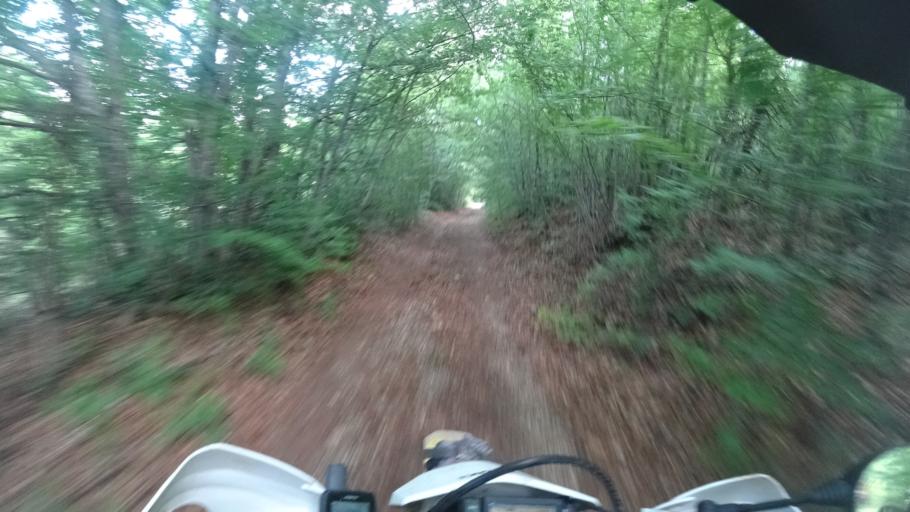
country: HR
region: Zadarska
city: Gracac
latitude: 44.2632
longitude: 15.9319
